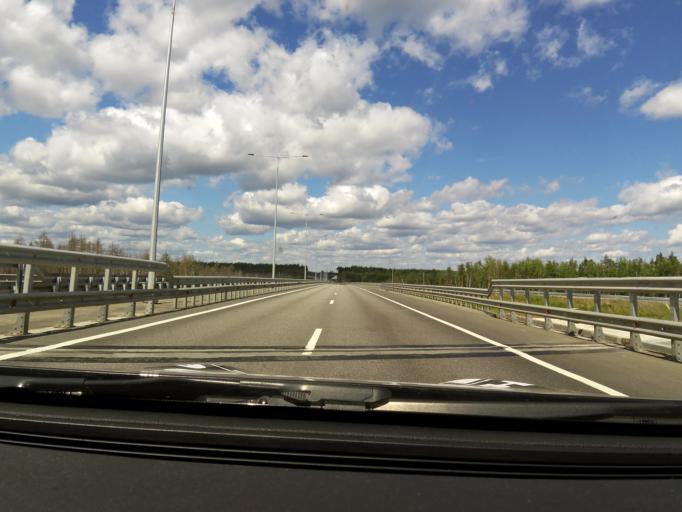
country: RU
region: Tverskaya
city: Vyshniy Volochek
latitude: 57.4162
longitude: 34.5091
